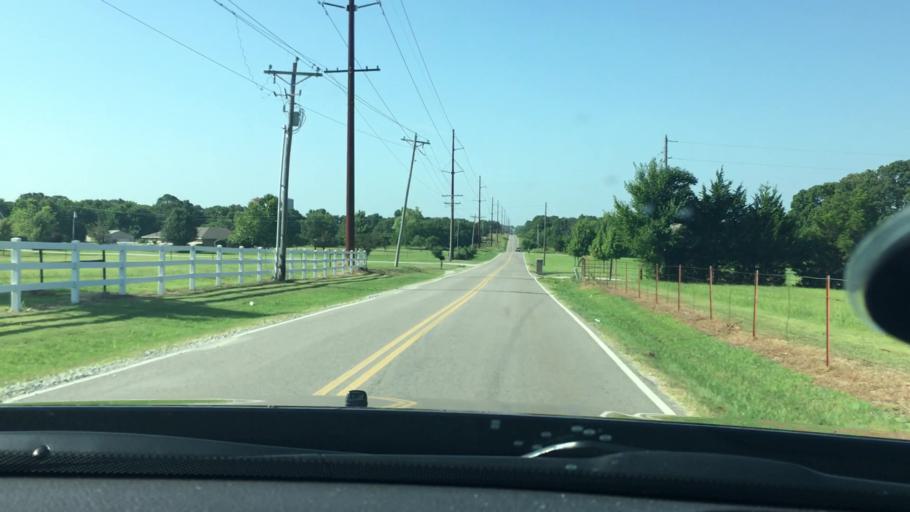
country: US
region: Oklahoma
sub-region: Pontotoc County
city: Ada
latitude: 34.8092
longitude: -96.6348
